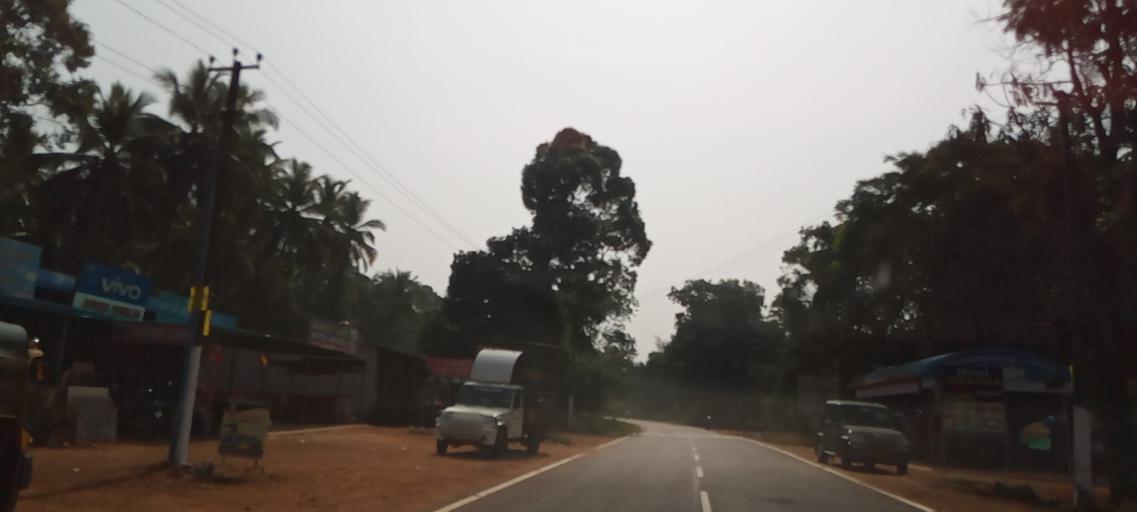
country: IN
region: Karnataka
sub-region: Udupi
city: Someshwar
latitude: 13.5179
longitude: 74.9348
